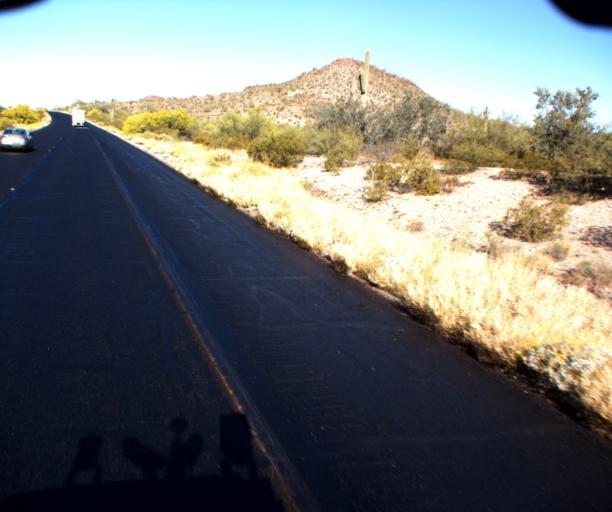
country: US
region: Arizona
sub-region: Pinal County
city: Maricopa
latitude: 32.8485
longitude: -112.3082
